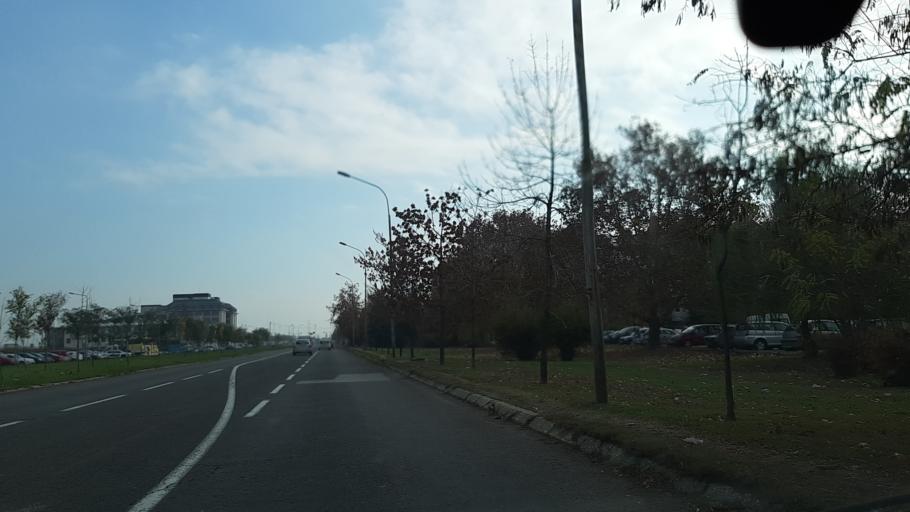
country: MK
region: Kisela Voda
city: Usje
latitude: 41.9914
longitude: 21.4684
